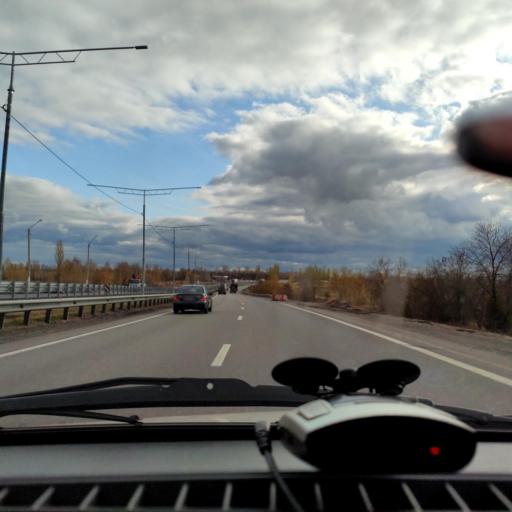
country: RU
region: Voronezj
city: Ramon'
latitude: 51.9785
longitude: 39.2173
